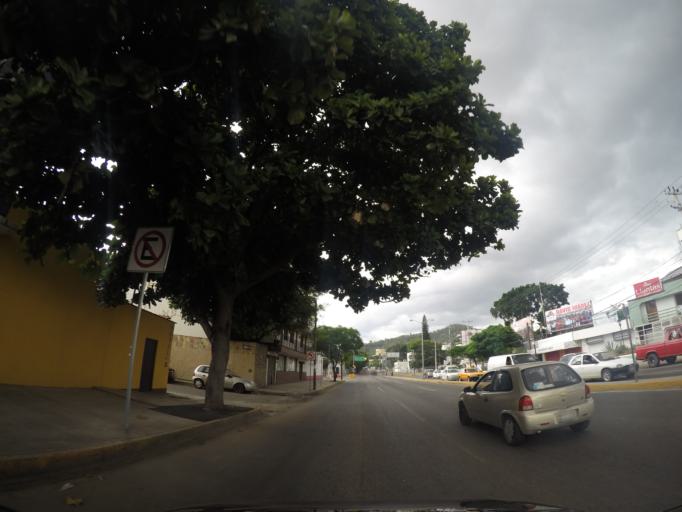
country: MX
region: Oaxaca
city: Oaxaca de Juarez
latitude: 17.0713
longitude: -96.7188
